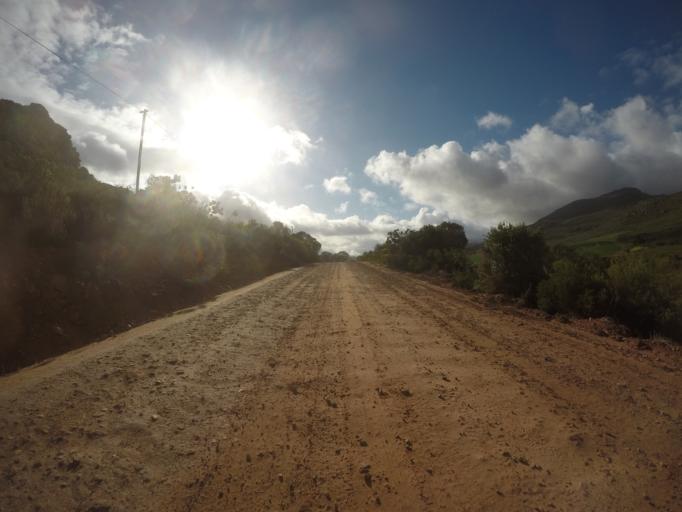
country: ZA
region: Western Cape
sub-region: West Coast District Municipality
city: Clanwilliam
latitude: -32.3434
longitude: 18.8164
